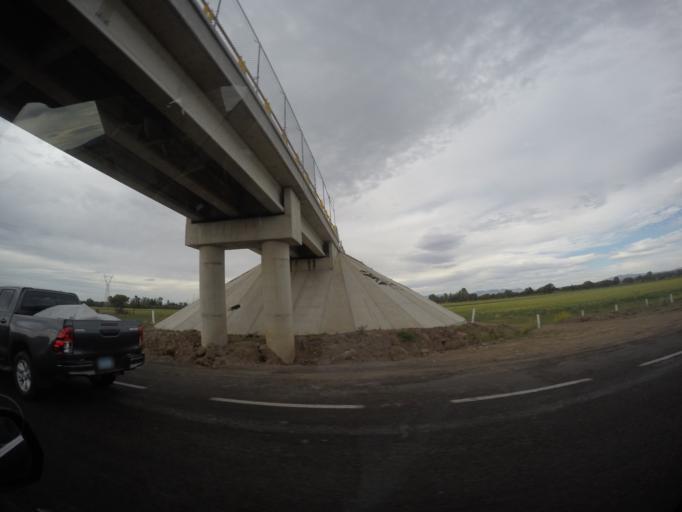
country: MX
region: Guanajuato
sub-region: Irapuato
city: Serrano
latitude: 20.7898
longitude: -101.4215
